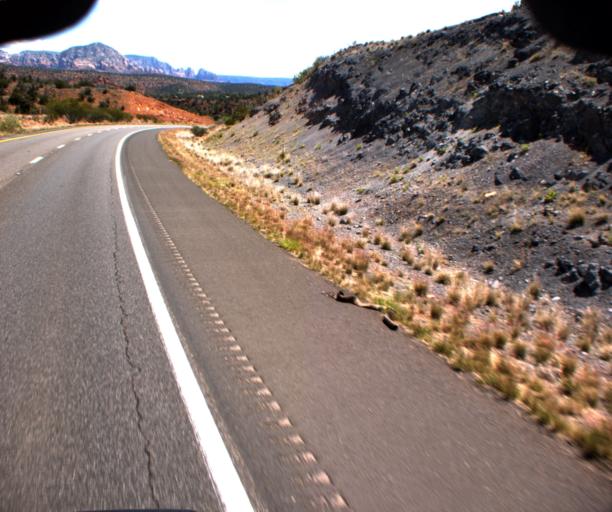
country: US
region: Arizona
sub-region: Yavapai County
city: West Sedona
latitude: 34.8372
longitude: -111.8877
